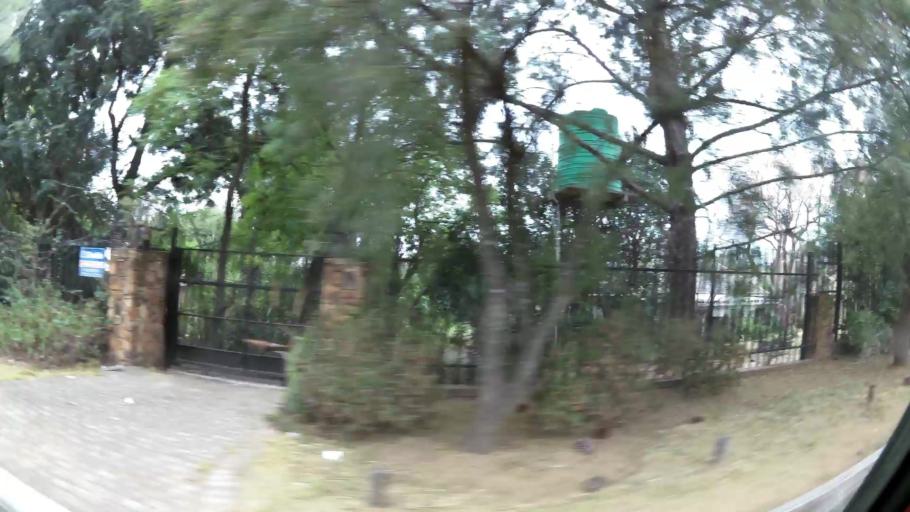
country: ZA
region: Gauteng
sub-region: City of Johannesburg Metropolitan Municipality
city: Roodepoort
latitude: -26.0957
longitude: 27.9100
